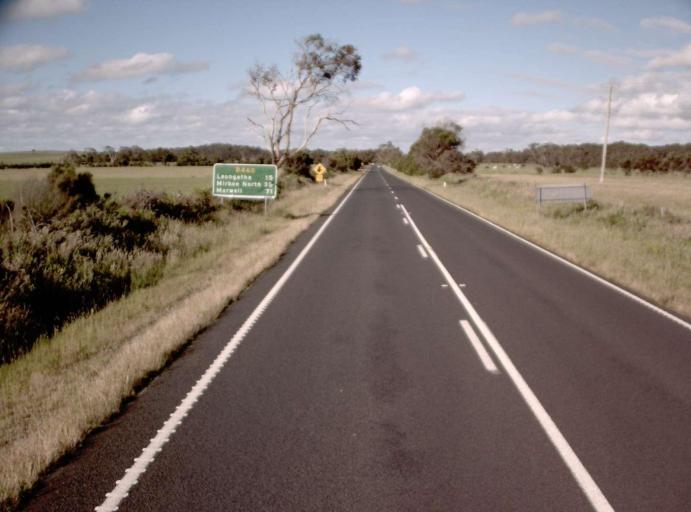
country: AU
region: Victoria
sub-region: Bass Coast
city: North Wonthaggi
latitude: -38.5767
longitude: 145.8310
